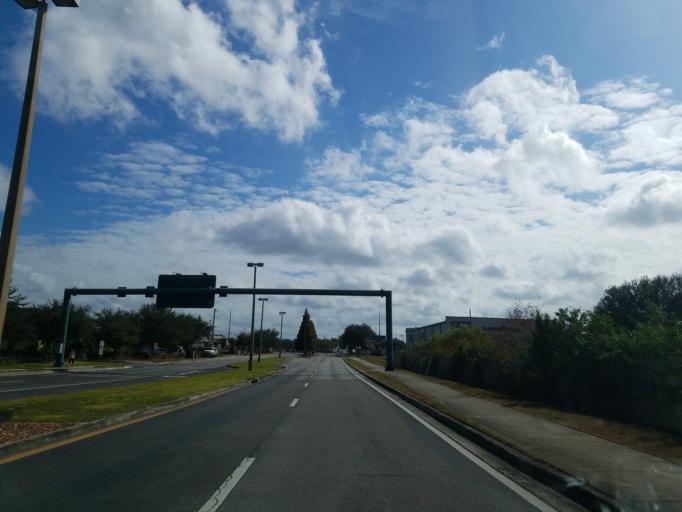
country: US
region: Florida
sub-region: Hillsborough County
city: Brandon
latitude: 27.9268
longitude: -82.3185
